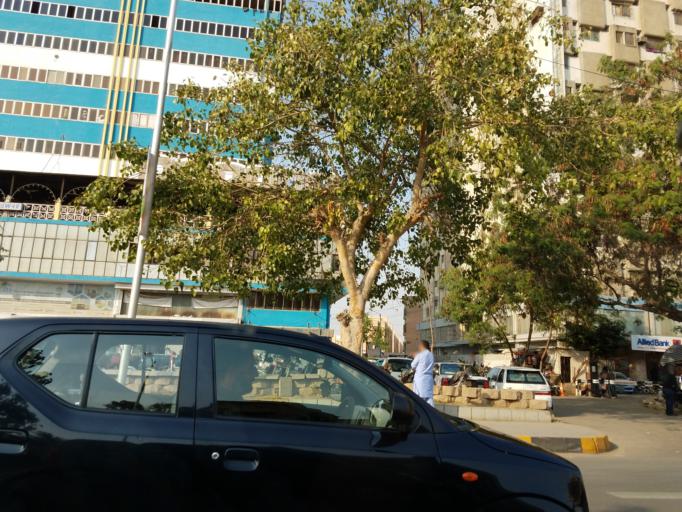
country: PK
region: Sindh
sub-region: Karachi District
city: Karachi
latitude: 24.8573
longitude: 67.0461
